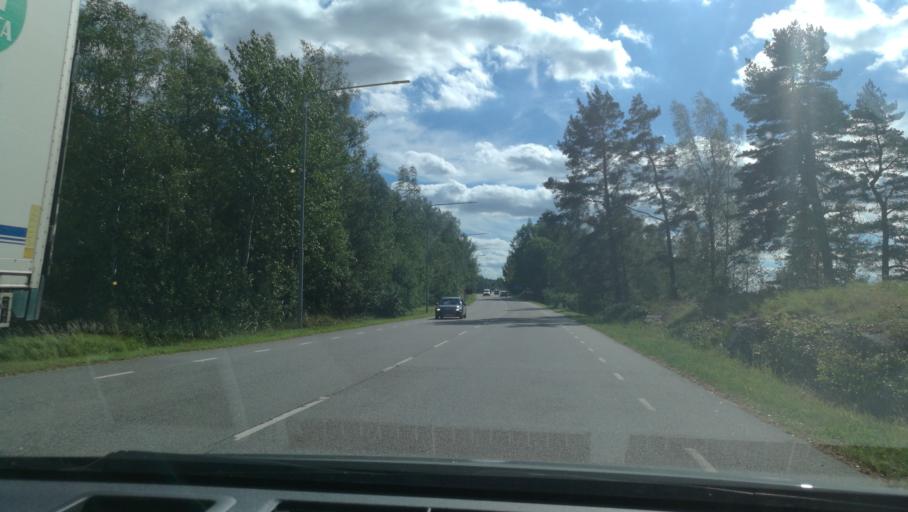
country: SE
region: Vaestra Goetaland
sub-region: Mariestads Kommun
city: Mariestad
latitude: 58.6900
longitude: 13.8426
